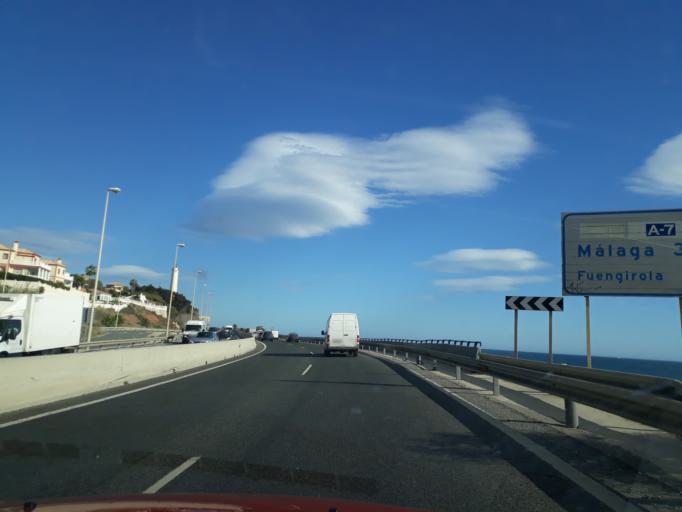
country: ES
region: Andalusia
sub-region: Provincia de Malaga
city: Fuengirola
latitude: 36.5068
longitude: -4.6437
